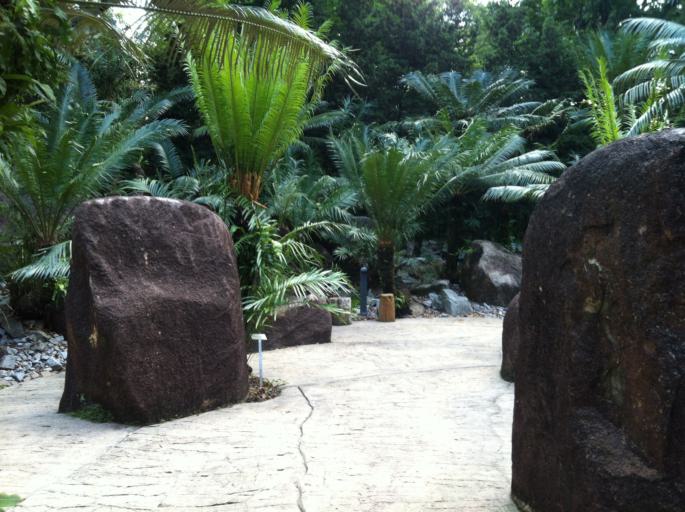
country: SG
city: Singapore
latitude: 1.3164
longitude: 103.8157
